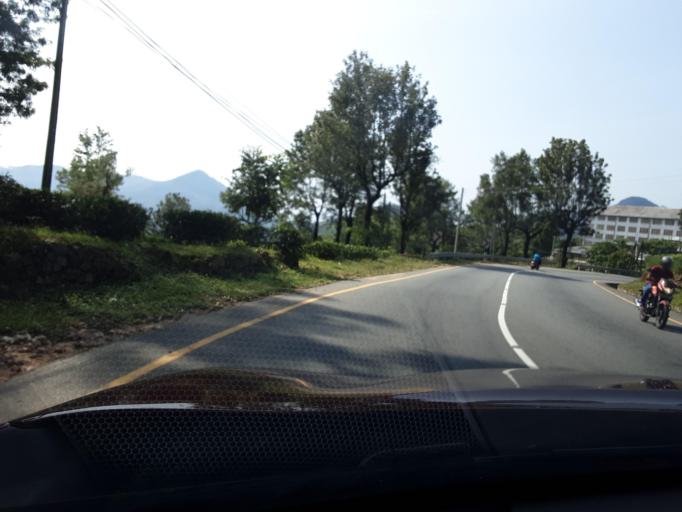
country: LK
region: Uva
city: Badulla
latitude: 6.9521
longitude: 81.1237
